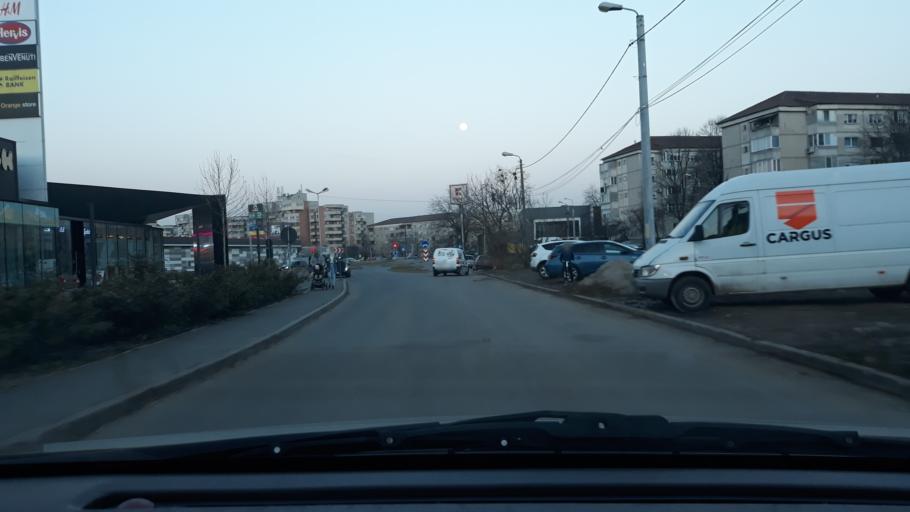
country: RO
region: Bihor
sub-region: Comuna Biharea
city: Oradea
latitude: 47.0576
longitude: 21.9139
